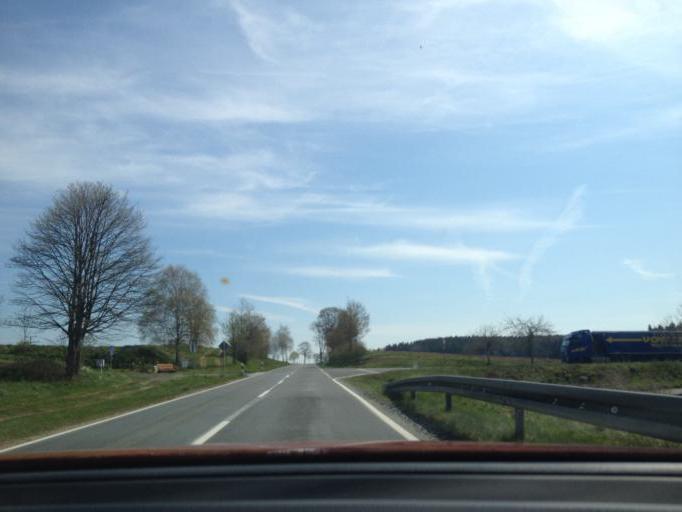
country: DE
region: Bavaria
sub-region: Upper Franconia
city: Roslau
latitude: 50.0787
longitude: 11.9896
